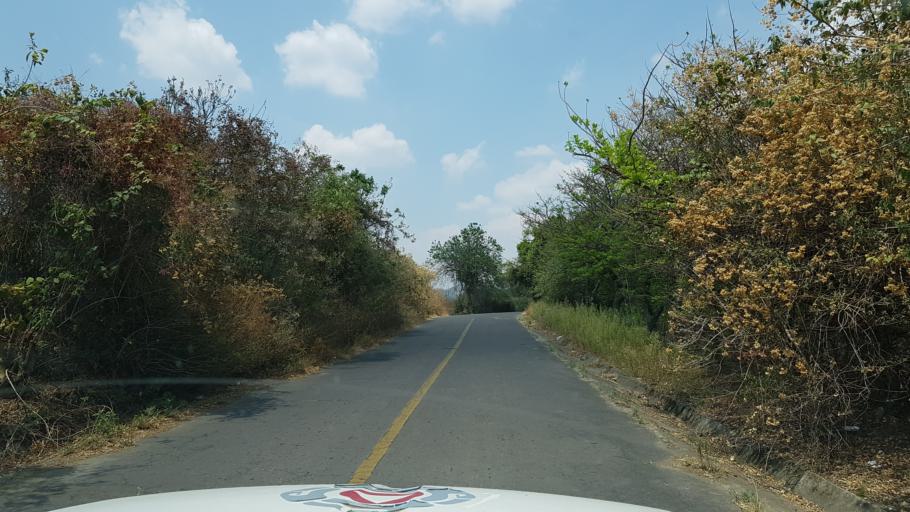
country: MX
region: Morelos
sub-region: Yecapixtla
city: Texcala
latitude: 18.9217
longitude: -98.8083
